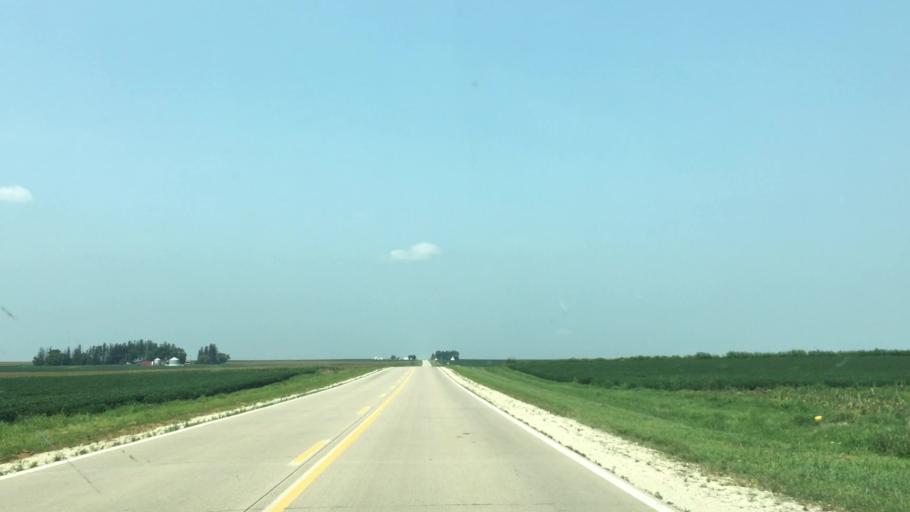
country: US
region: Iowa
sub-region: Fayette County
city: Oelwein
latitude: 42.6933
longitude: -91.8051
